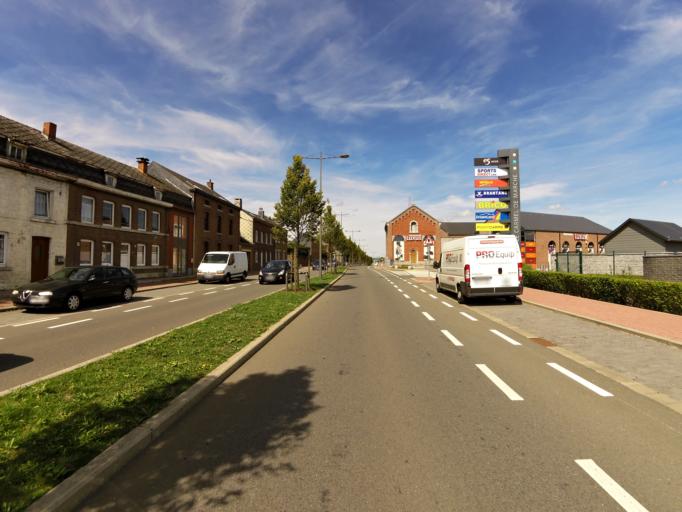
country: BE
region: Wallonia
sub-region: Province du Luxembourg
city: Marche-en-Famenne
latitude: 50.2350
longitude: 5.3445
